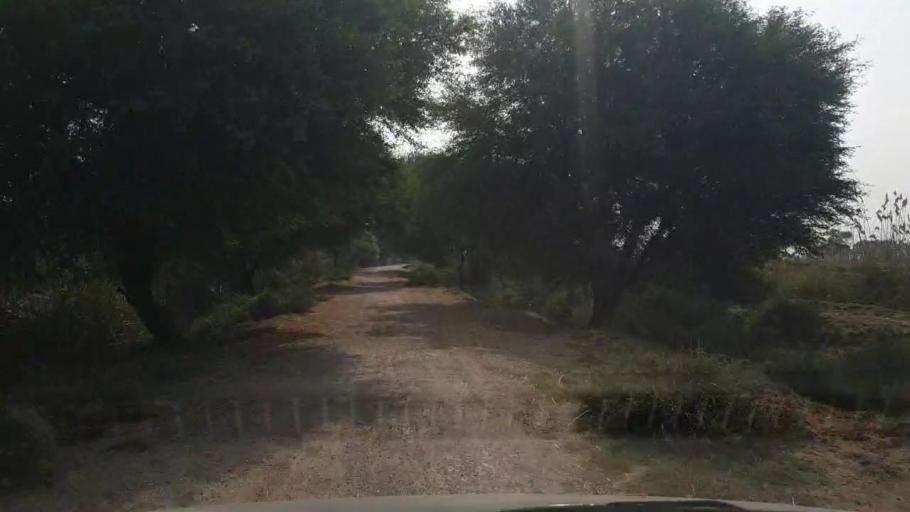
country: PK
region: Sindh
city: Tando Muhammad Khan
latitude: 25.1234
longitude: 68.4374
